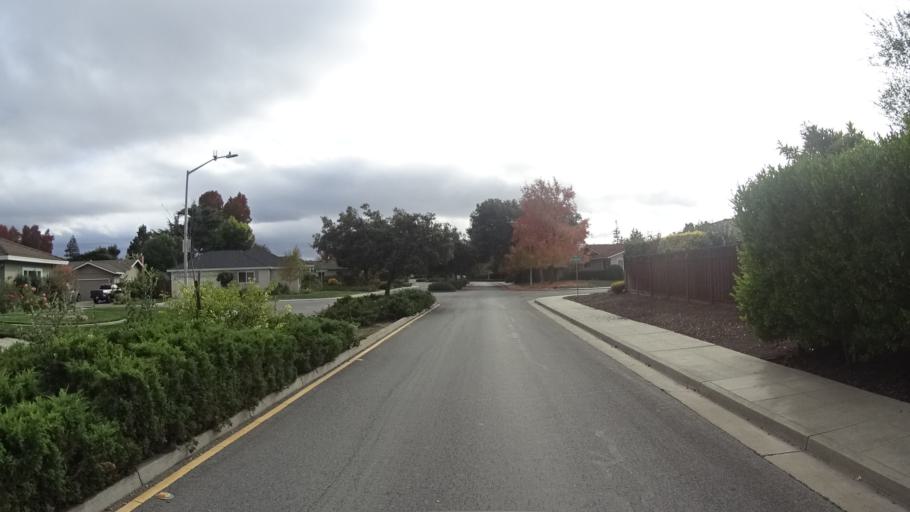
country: US
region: California
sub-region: Santa Clara County
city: Santa Clara
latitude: 37.3322
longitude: -121.9696
